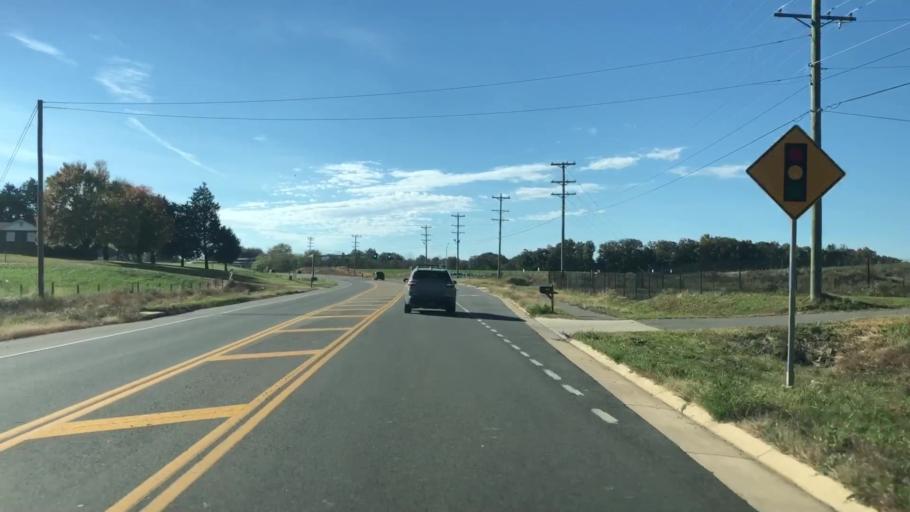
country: US
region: Virginia
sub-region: Prince William County
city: Gainesville
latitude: 38.7531
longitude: -77.6194
